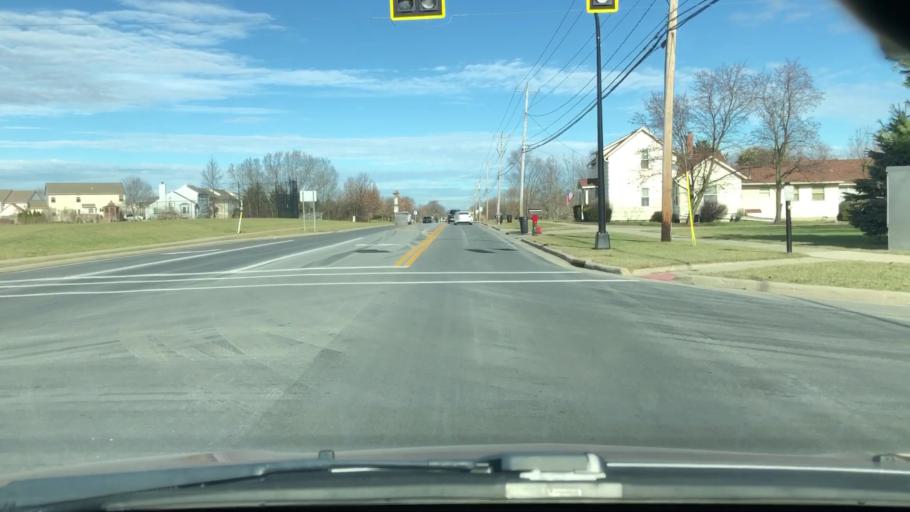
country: US
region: Ohio
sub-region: Franklin County
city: Westerville
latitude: 40.1561
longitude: -82.9006
